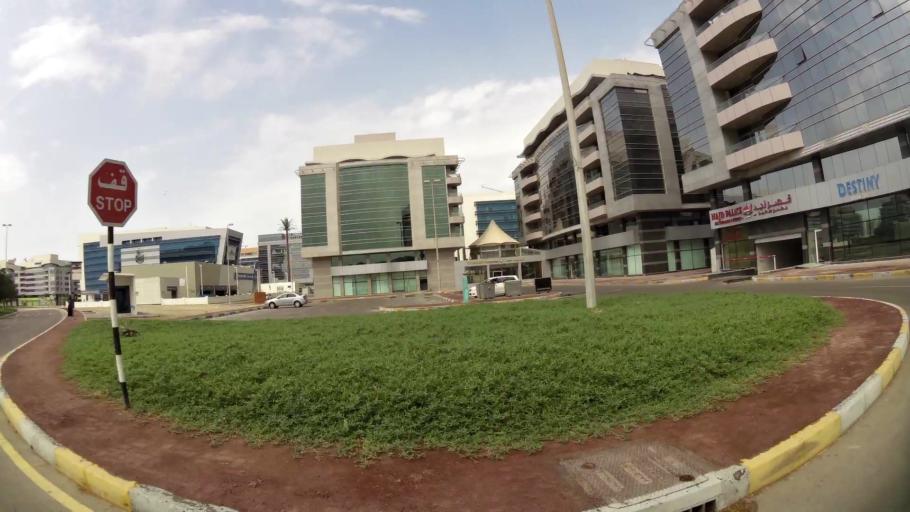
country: AE
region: Abu Dhabi
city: Abu Dhabi
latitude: 24.4297
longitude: 54.4669
